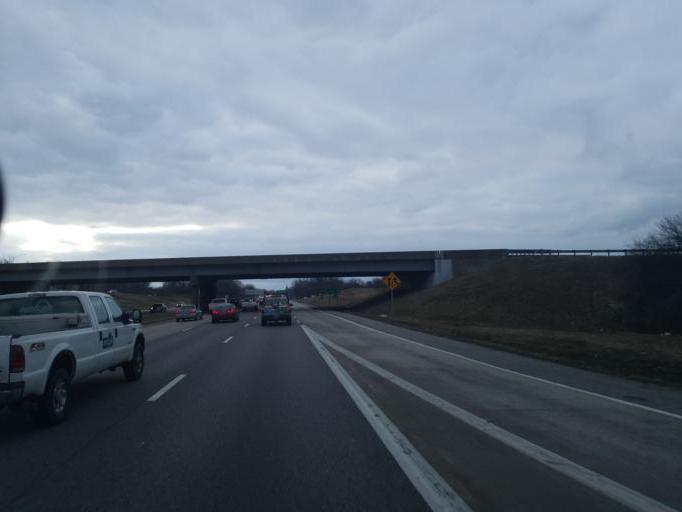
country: US
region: Missouri
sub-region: Saint Charles County
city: Saint Peters
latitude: 38.8014
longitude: -90.6529
